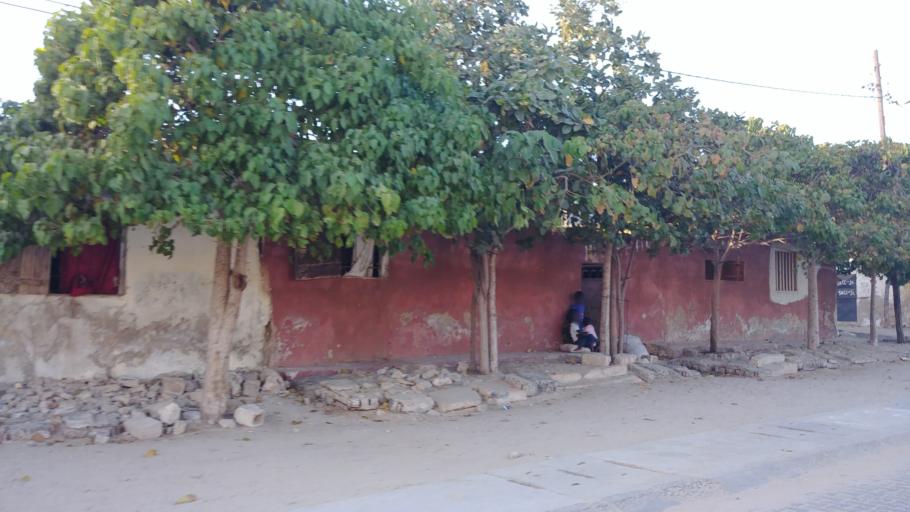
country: SN
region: Saint-Louis
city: Saint-Louis
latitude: 16.0203
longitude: -16.4969
